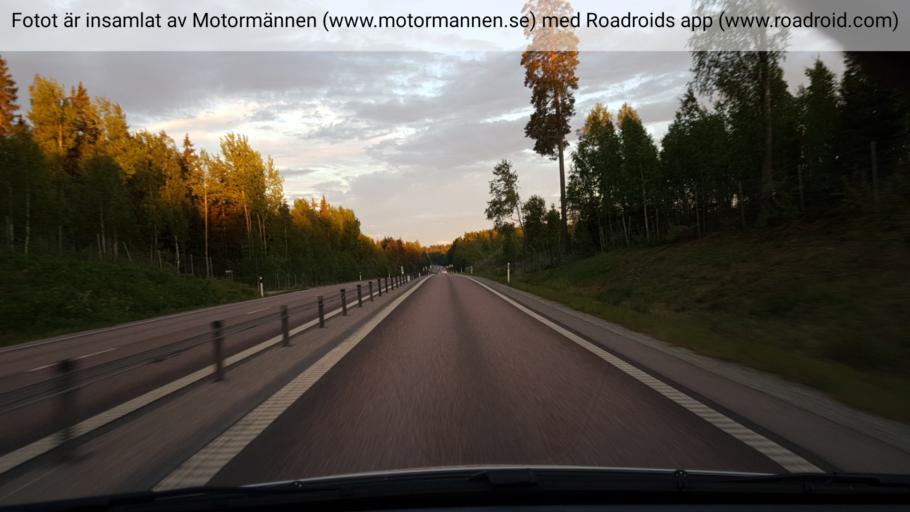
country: SE
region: Vaestmanland
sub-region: Norbergs Kommun
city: Norberg
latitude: 59.9176
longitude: 15.9530
